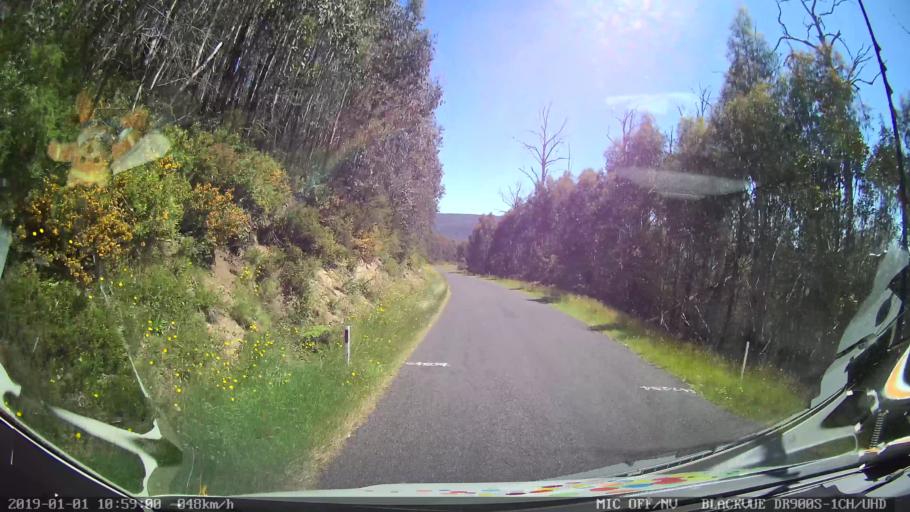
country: AU
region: New South Wales
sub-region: Snowy River
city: Jindabyne
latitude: -35.9884
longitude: 148.3985
